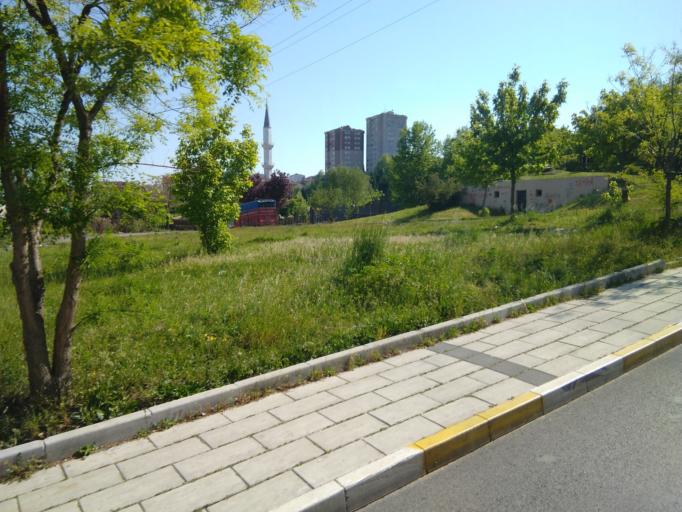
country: TR
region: Istanbul
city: Mahmutbey
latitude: 41.0459
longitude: 28.7972
